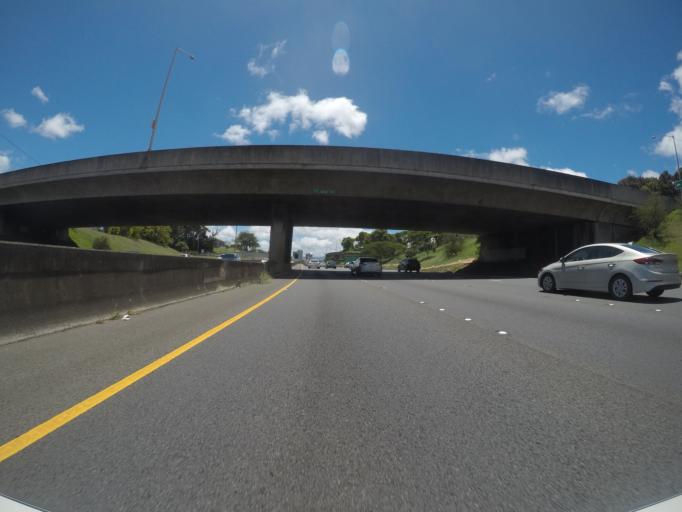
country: US
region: Hawaii
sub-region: Honolulu County
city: Halawa Heights
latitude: 21.3426
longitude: -157.8880
